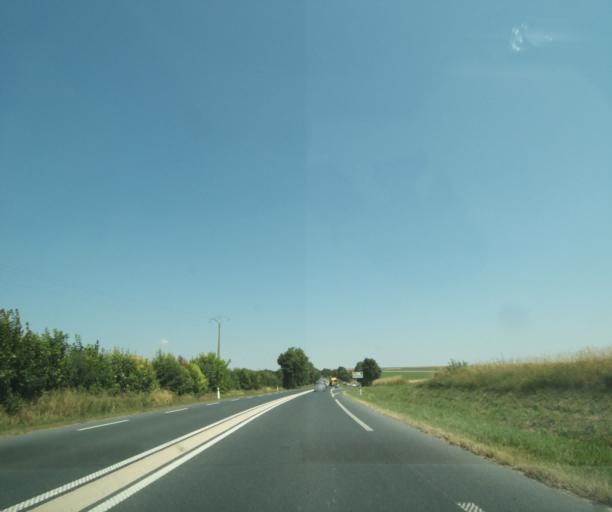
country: FR
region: Champagne-Ardenne
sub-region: Departement de la Marne
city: Mourmelon-le-Grand
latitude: 49.0616
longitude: 4.2971
